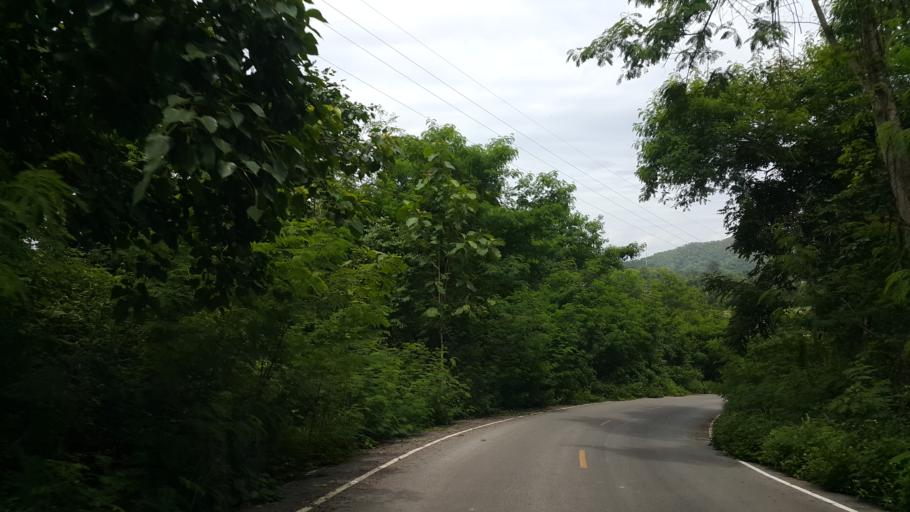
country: TH
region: Lampang
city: Mueang Pan
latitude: 18.7848
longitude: 99.5120
